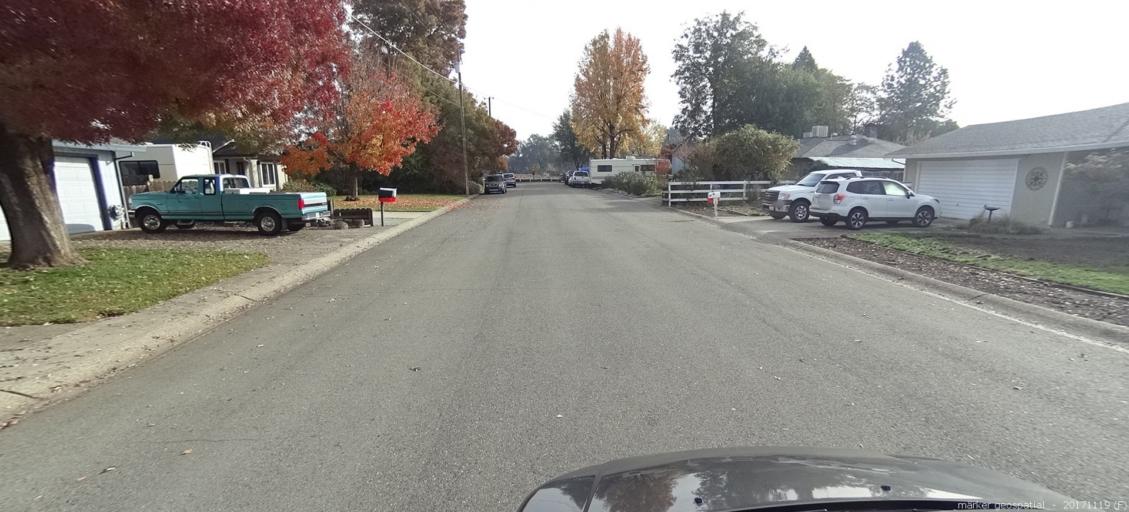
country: US
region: California
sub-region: Shasta County
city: Anderson
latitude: 40.5173
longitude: -122.3314
